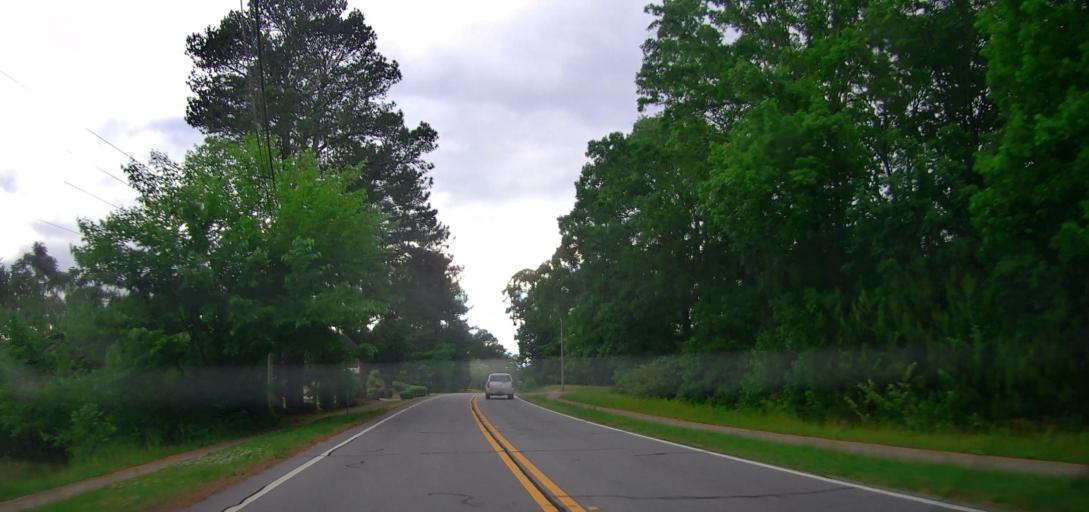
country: US
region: Georgia
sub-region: Clarke County
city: Country Club Estates
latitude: 33.9339
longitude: -83.4394
